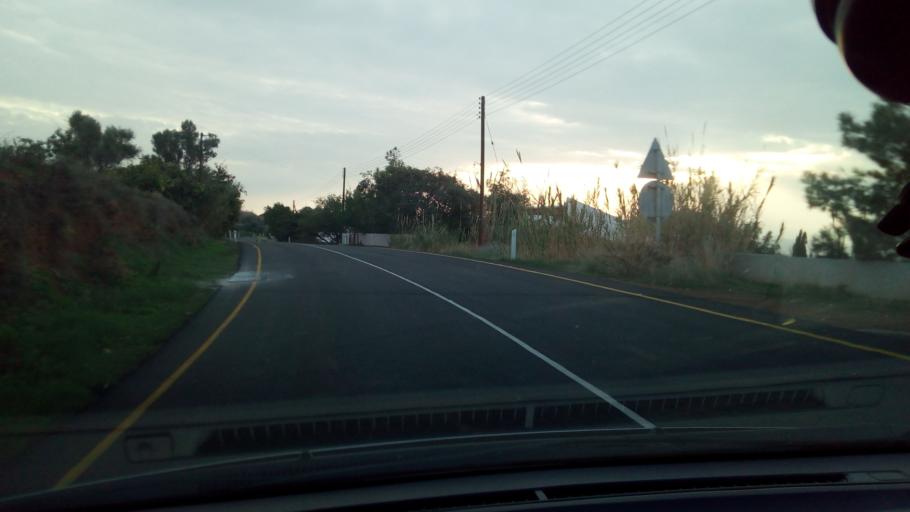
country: CY
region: Pafos
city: Polis
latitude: 35.1390
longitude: 32.5226
